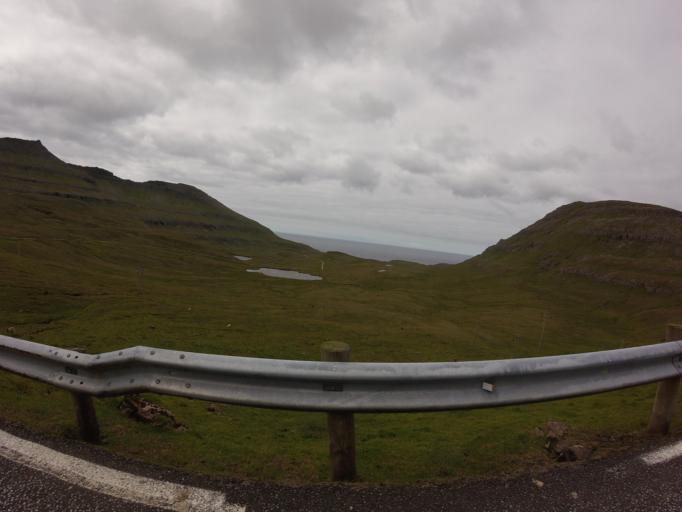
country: FO
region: Suduroy
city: Tvoroyri
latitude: 61.5191
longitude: -6.8368
